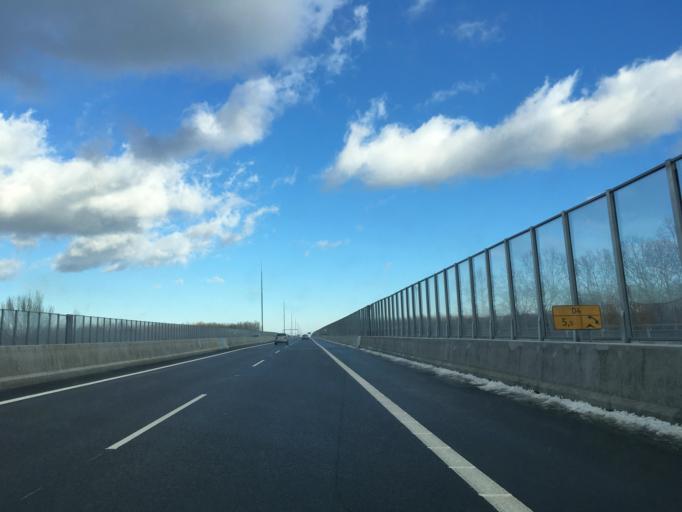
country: SK
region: Bratislavsky
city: Bratislava
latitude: 48.0805
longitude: 17.1425
